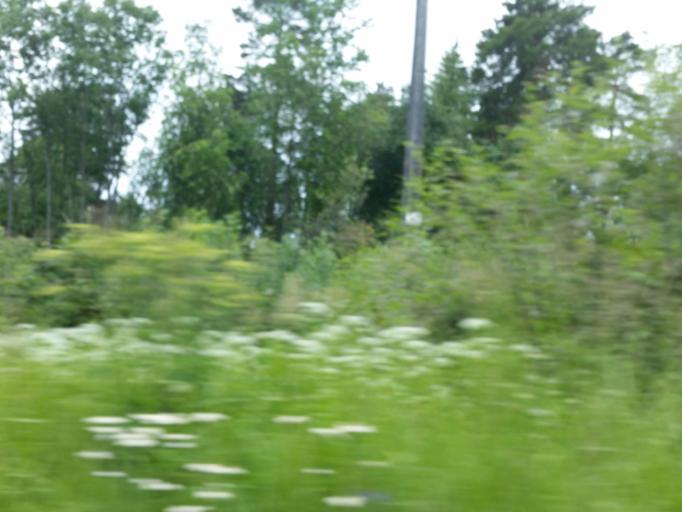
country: FI
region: Northern Savo
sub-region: Kuopio
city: Kuopio
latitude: 62.9046
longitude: 27.7019
